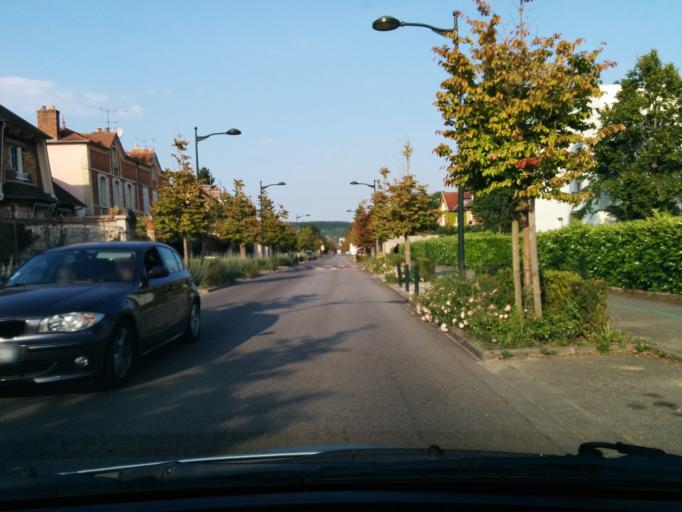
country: FR
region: Haute-Normandie
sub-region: Departement de l'Eure
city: Vernon
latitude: 49.0891
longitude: 1.4698
